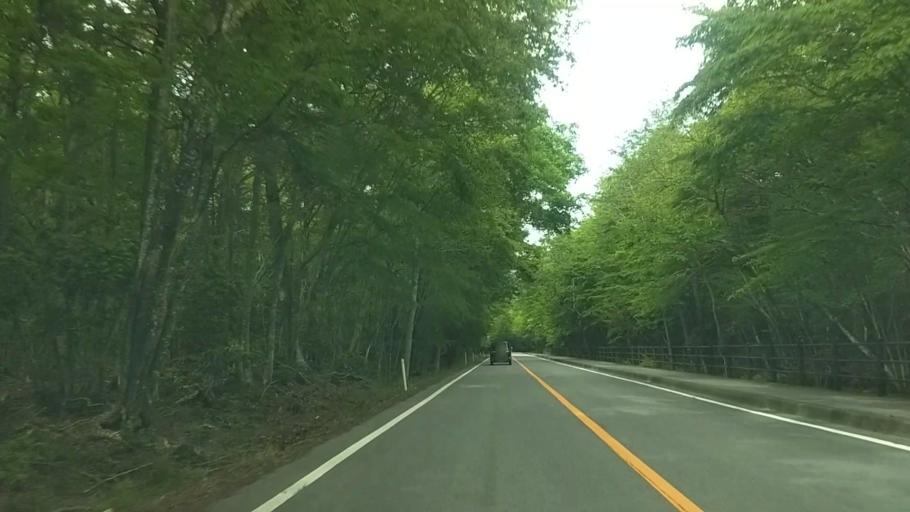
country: JP
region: Yamanashi
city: Fujikawaguchiko
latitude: 35.4887
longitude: 138.6449
